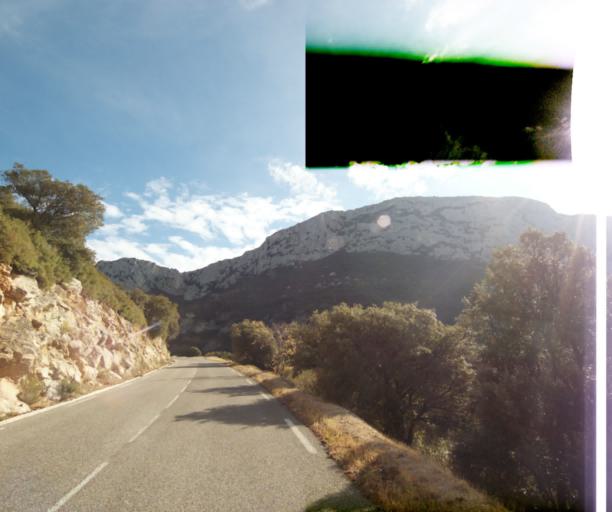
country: FR
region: Provence-Alpes-Cote d'Azur
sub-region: Departement des Bouches-du-Rhone
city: Gemenos
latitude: 43.3022
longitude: 5.6653
